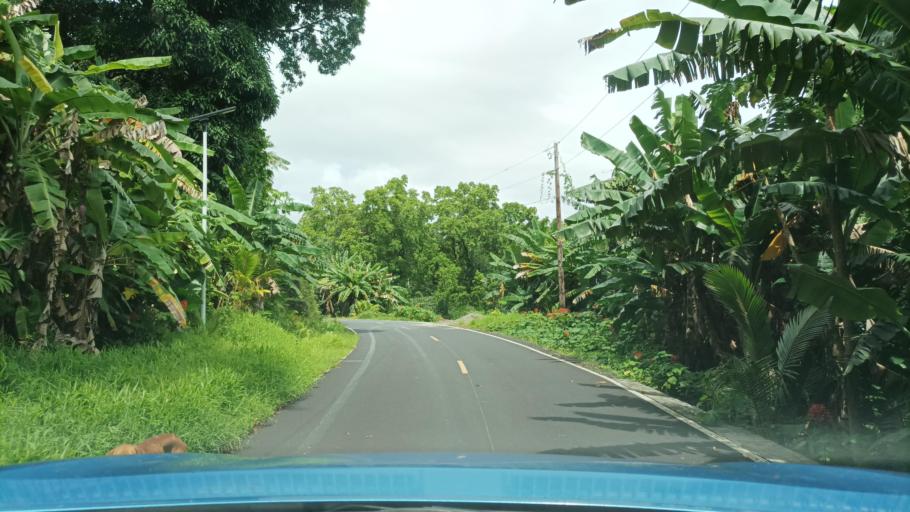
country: FM
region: Pohnpei
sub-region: Madolenihm Municipality
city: Madolenihm Municipality Government
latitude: 6.8773
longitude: 158.3333
